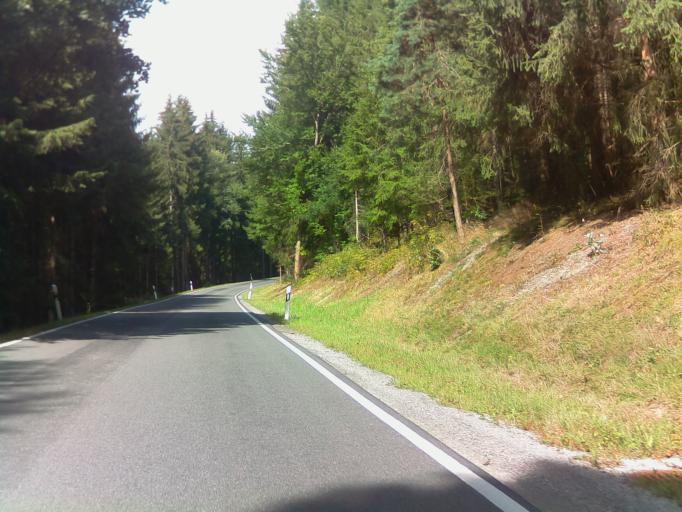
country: DE
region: Thuringia
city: Schwarza
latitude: 50.6352
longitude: 10.5284
